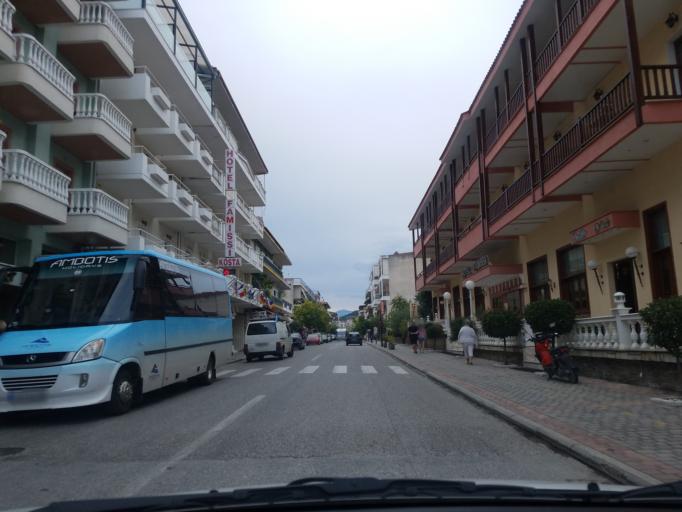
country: GR
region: Thessaly
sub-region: Trikala
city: Kalampaka
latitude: 39.7027
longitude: 21.6319
